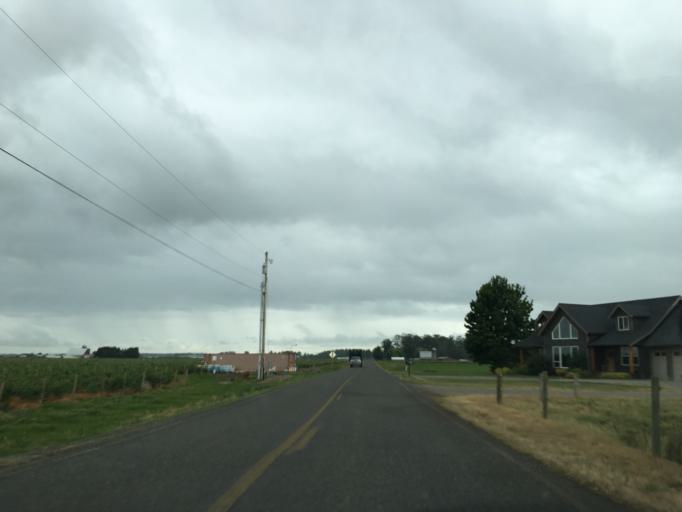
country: US
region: Washington
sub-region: Whatcom County
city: Lynden
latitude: 48.9789
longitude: -122.4295
